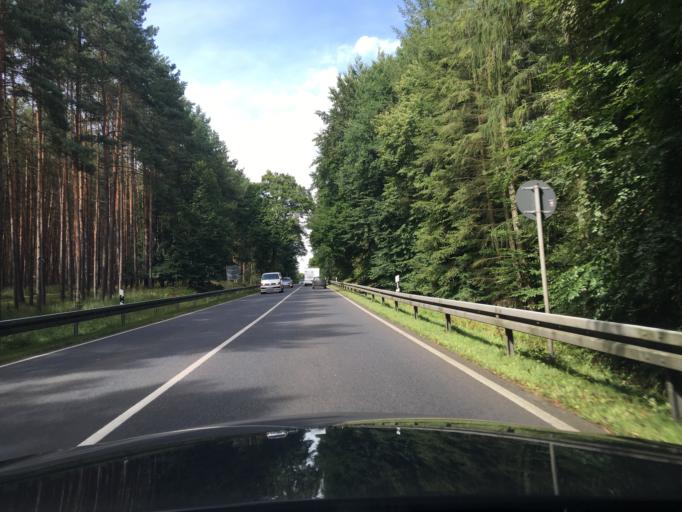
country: DE
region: Brandenburg
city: Furstenberg
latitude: 53.2631
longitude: 13.1167
